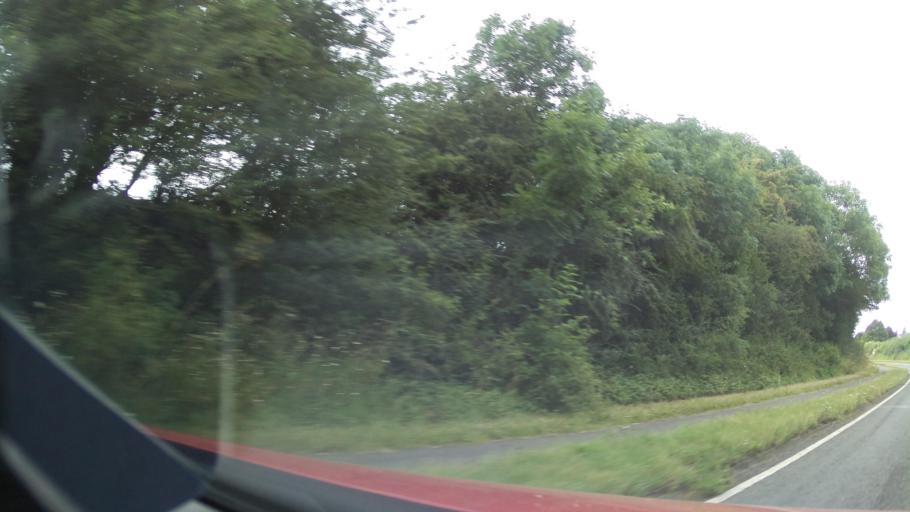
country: GB
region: England
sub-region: Lincolnshire
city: Stamford
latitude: 52.6401
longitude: -0.4868
